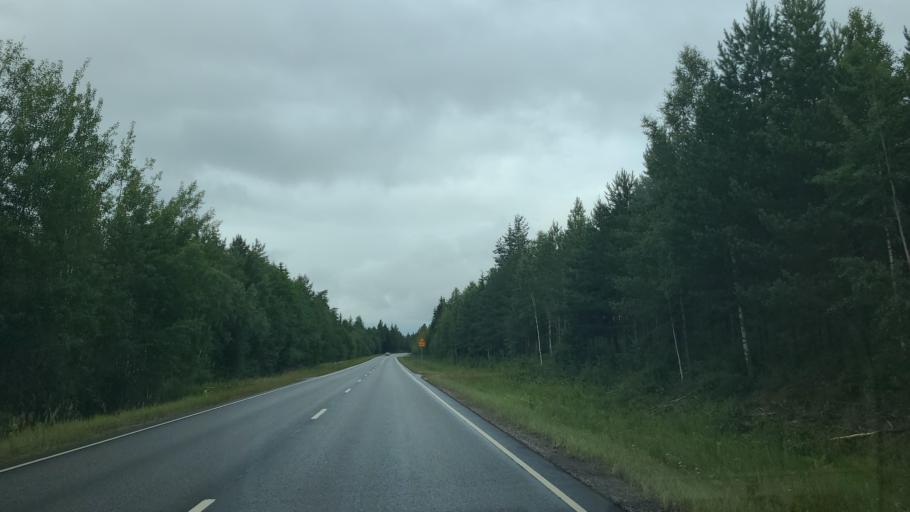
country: FI
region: Varsinais-Suomi
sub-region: Aboland-Turunmaa
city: Kimito
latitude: 60.2070
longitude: 22.6449
